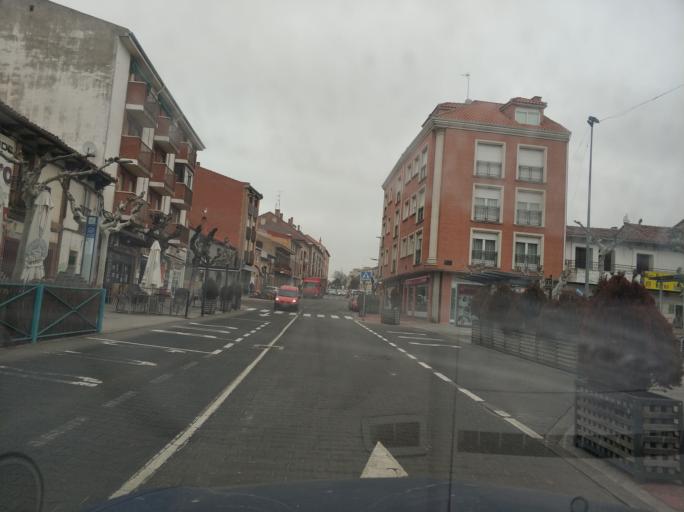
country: ES
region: Castille and Leon
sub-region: Provincia de Valladolid
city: Cisterniga
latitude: 41.6111
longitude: -4.6860
